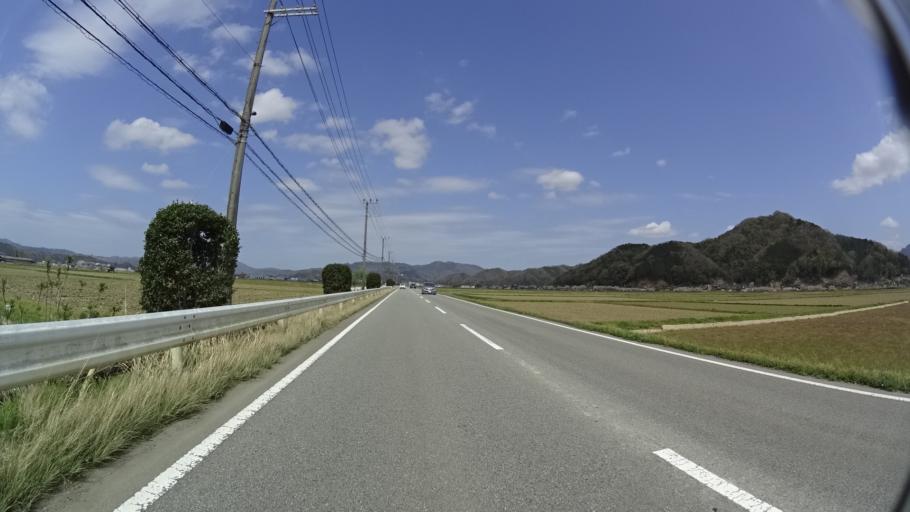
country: JP
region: Hyogo
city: Toyooka
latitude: 35.5144
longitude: 134.8400
